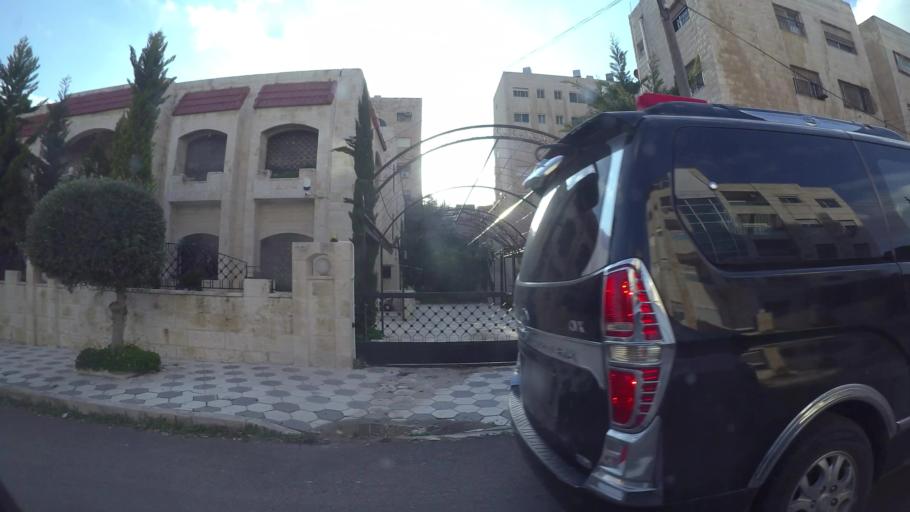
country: JO
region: Amman
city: Al Jubayhah
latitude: 32.0015
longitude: 35.8696
